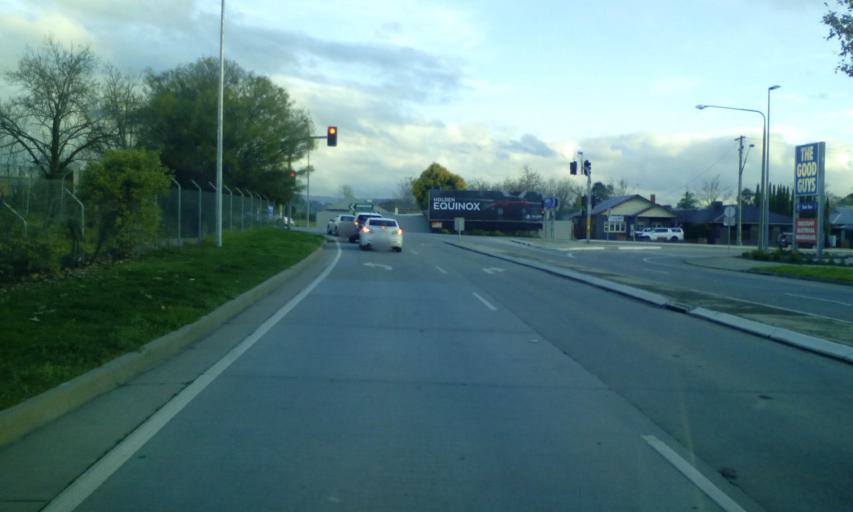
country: AU
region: New South Wales
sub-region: Albury Municipality
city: East Albury
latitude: -36.0851
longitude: 146.9230
